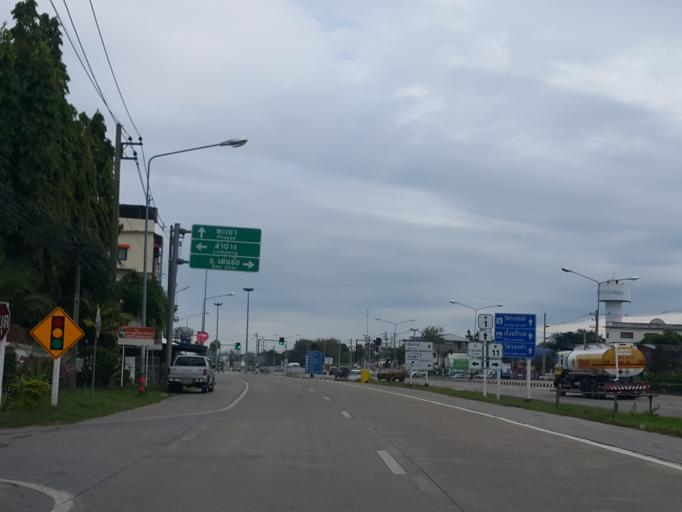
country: TH
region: Lampang
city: Lampang
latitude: 18.2842
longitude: 99.5114
